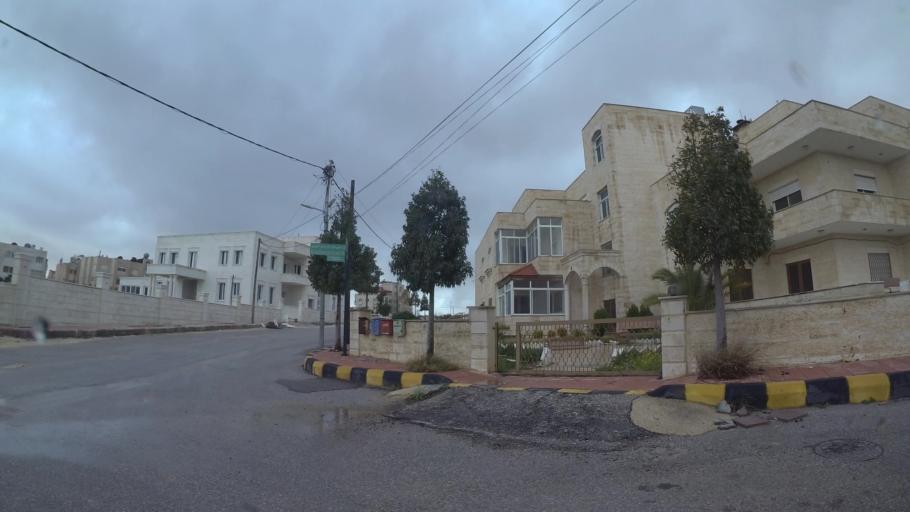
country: JO
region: Amman
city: Al Jubayhah
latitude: 32.0362
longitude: 35.8635
